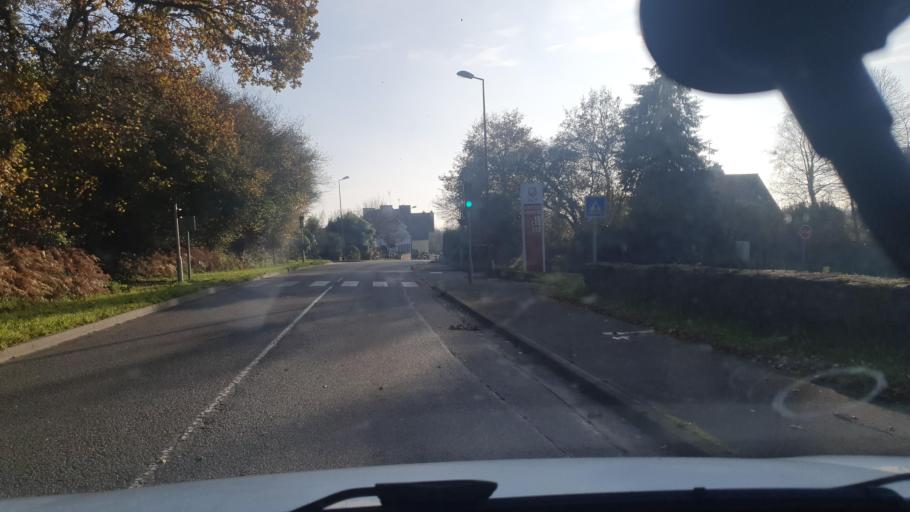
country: FR
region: Brittany
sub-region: Departement du Finistere
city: Briec
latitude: 48.0960
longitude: -4.0017
